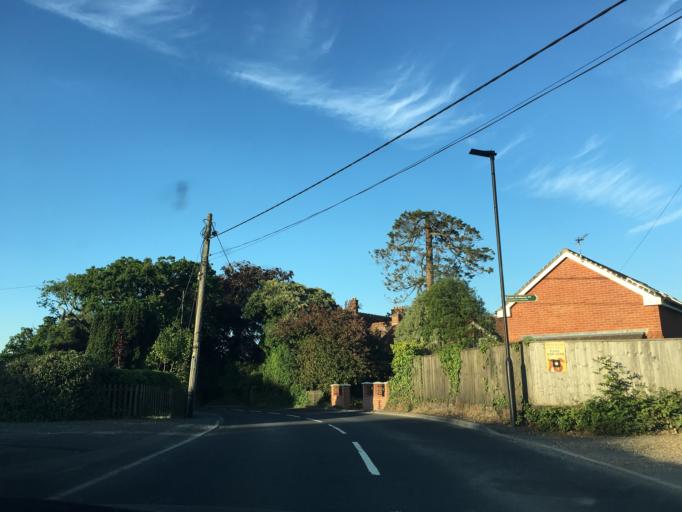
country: GB
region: England
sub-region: Isle of Wight
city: Newport
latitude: 50.7171
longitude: -1.2449
